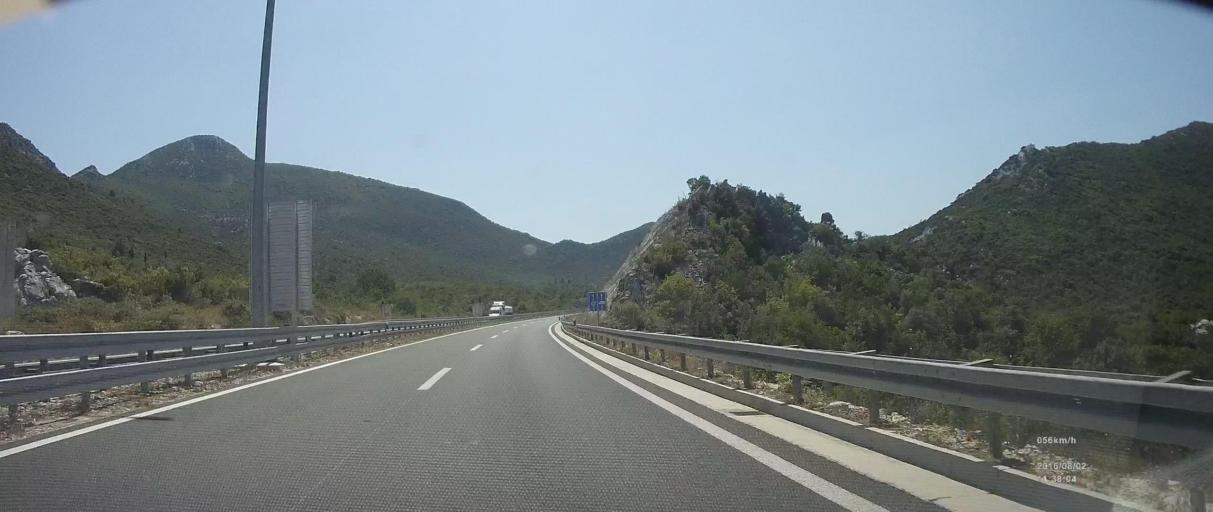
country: HR
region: Dubrovacko-Neretvanska
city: Komin
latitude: 43.0996
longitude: 17.4884
